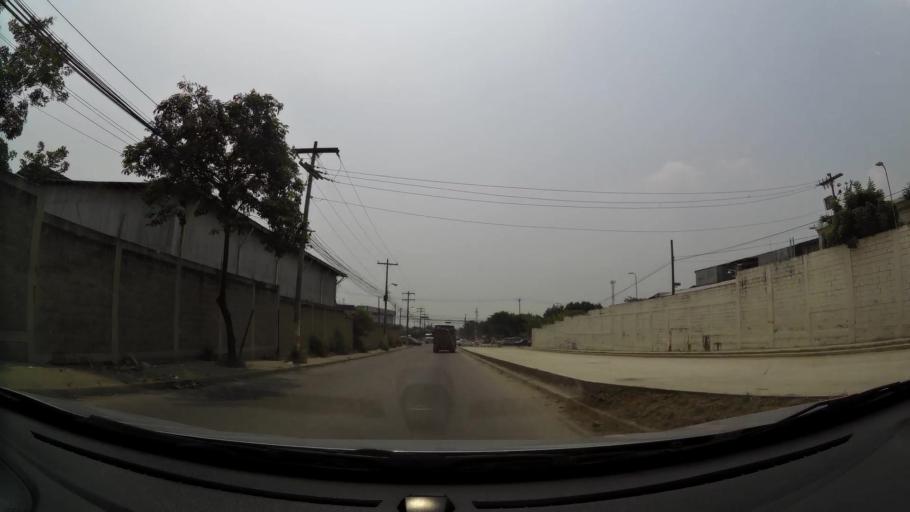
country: HN
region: Cortes
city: San Pedro Sula
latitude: 15.4834
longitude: -88.0259
